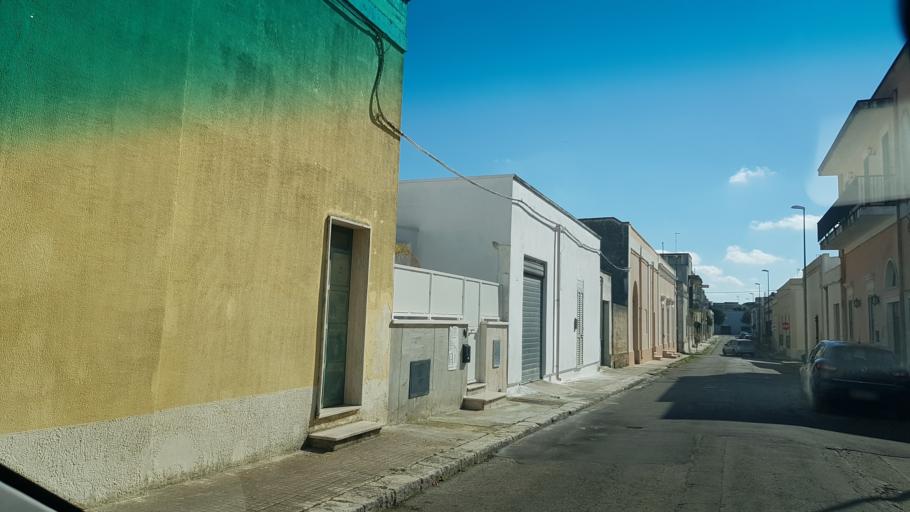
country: IT
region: Apulia
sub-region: Provincia di Lecce
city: Campi Salentina
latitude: 40.3969
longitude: 18.0144
